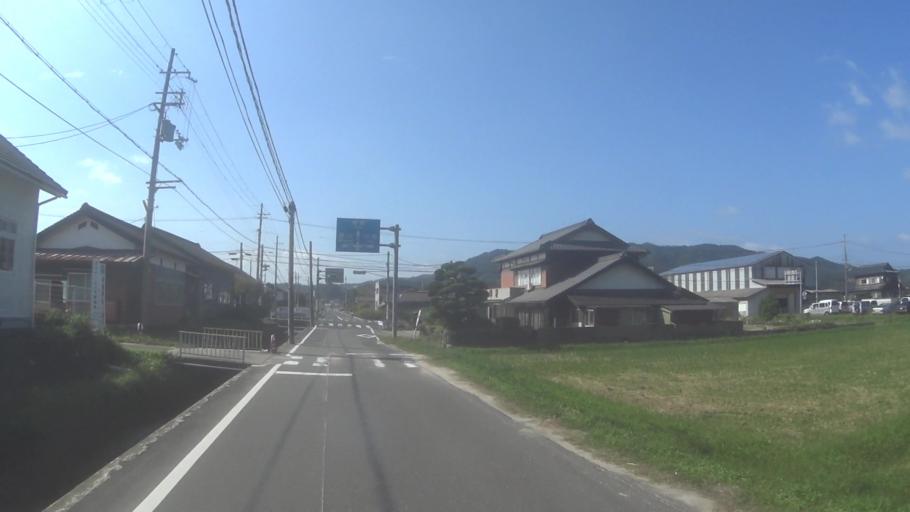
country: JP
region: Kyoto
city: Miyazu
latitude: 35.6799
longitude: 135.0995
